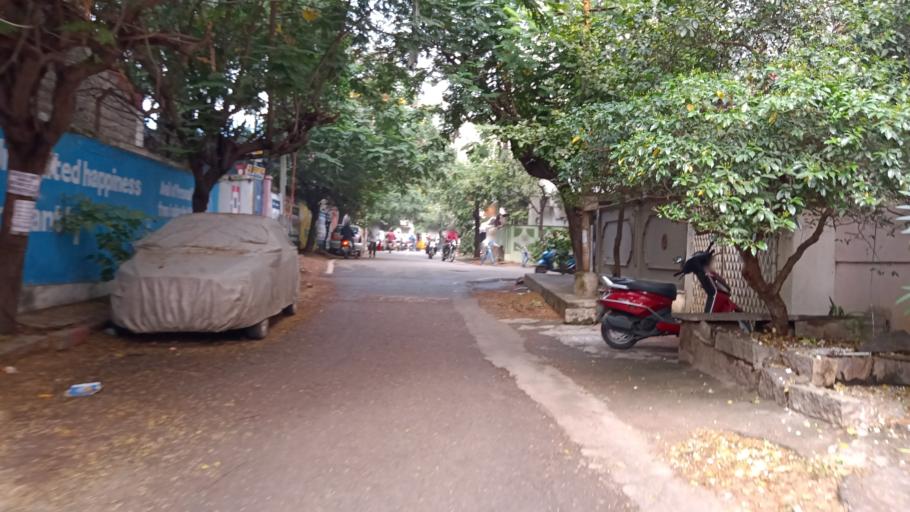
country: IN
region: Telangana
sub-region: Rangareddi
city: Kukatpalli
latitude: 17.4464
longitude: 78.4421
